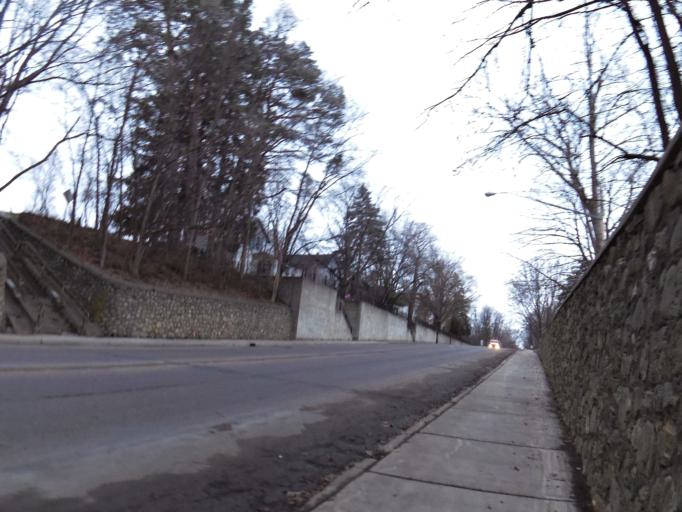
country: US
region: Wisconsin
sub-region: Saint Croix County
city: North Hudson
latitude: 44.9863
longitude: -92.7574
